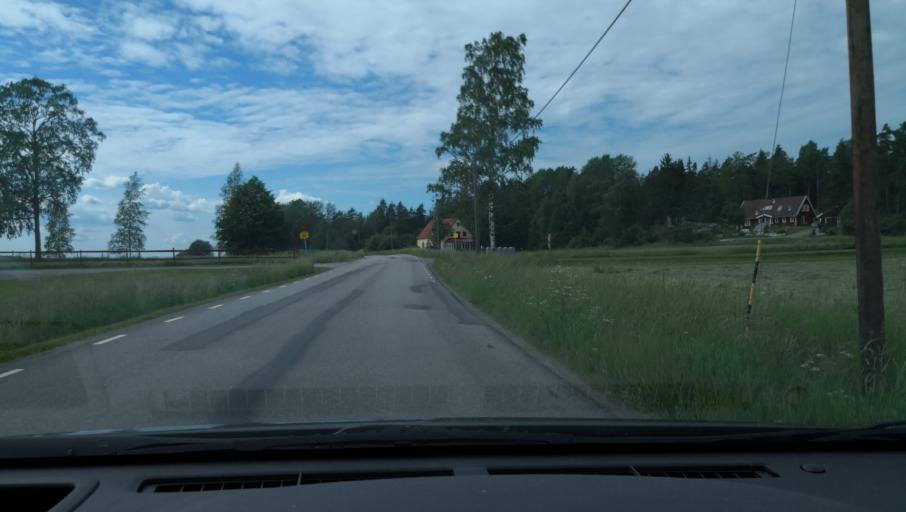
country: SE
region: Uppsala
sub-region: Uppsala Kommun
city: Uppsala
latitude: 59.8089
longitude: 17.5207
